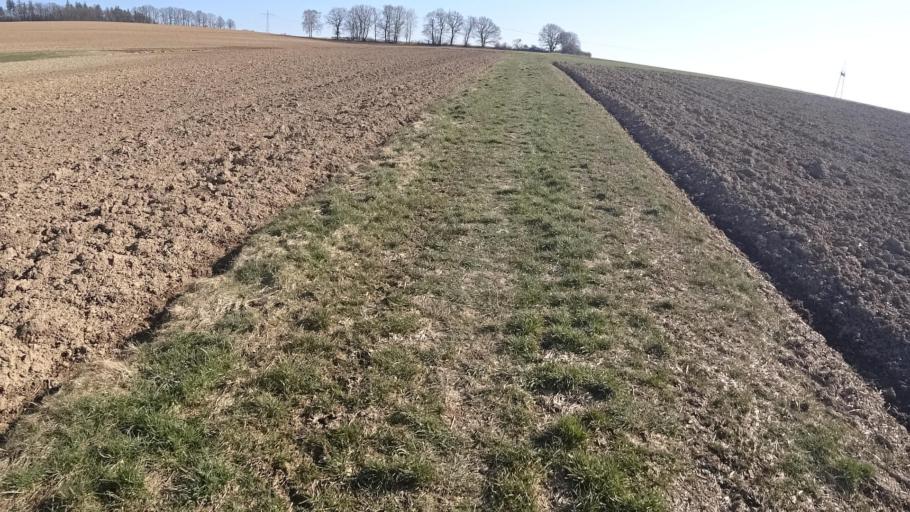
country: DE
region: Rheinland-Pfalz
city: Mutterschied
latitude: 49.9903
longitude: 7.5620
